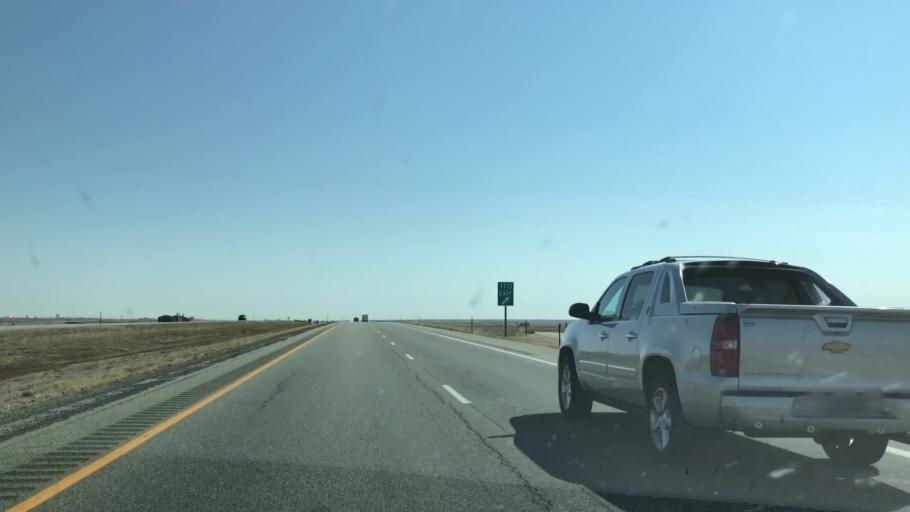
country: US
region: Wyoming
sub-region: Carbon County
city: Rawlins
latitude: 41.6646
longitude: -108.0360
